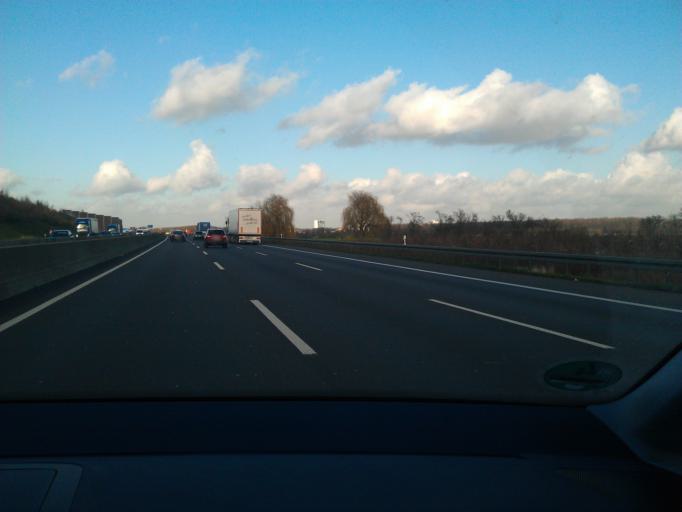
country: DE
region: North Rhine-Westphalia
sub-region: Regierungsbezirk Koln
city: Mengenich
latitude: 50.9563
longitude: 6.8505
